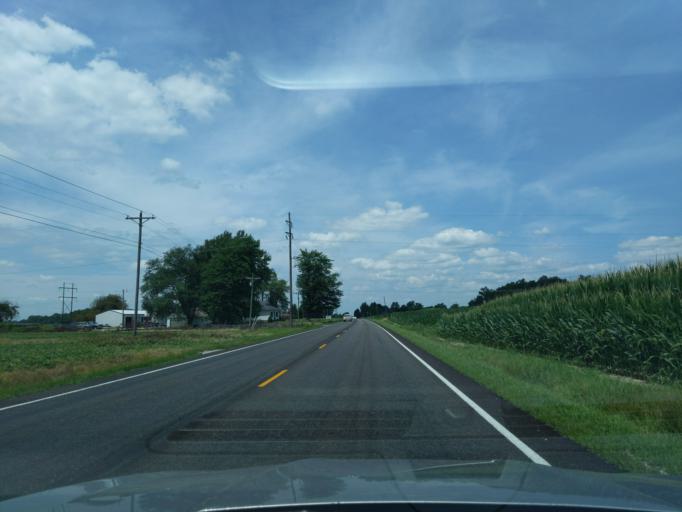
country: US
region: Indiana
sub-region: Ripley County
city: Osgood
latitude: 39.2157
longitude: -85.3332
